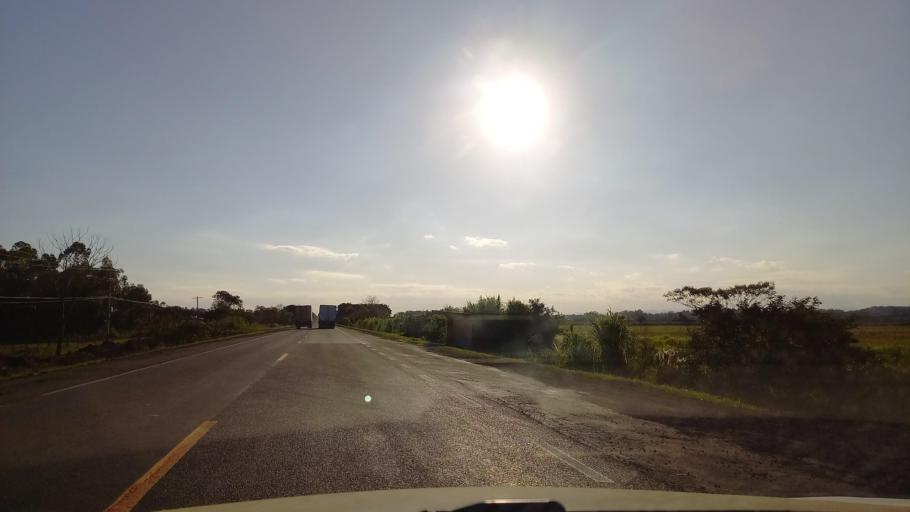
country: BR
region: Rio Grande do Sul
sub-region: Venancio Aires
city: Venancio Aires
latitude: -29.6638
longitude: -52.0589
